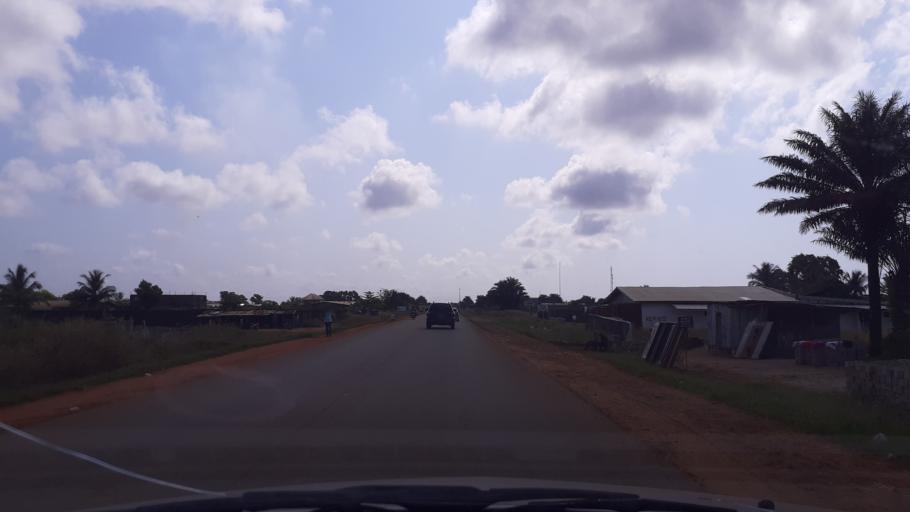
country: LR
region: Montserrado
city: Monrovia
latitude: 6.2217
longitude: -10.5987
